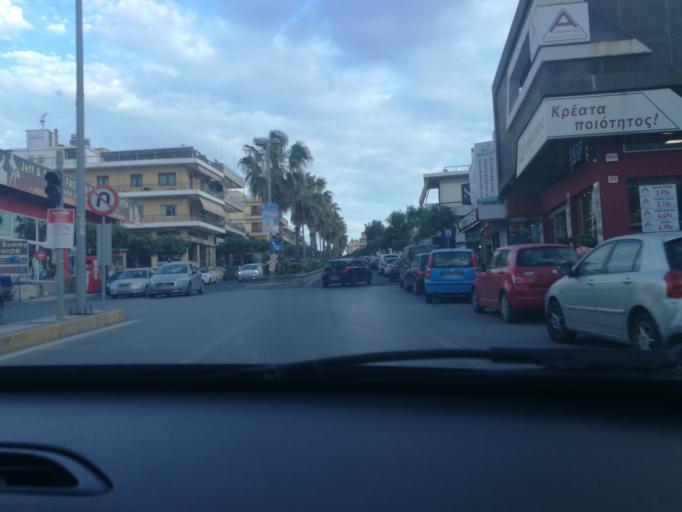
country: GR
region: Crete
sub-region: Nomos Irakleiou
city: Irakleion
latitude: 35.3200
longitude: 25.1440
